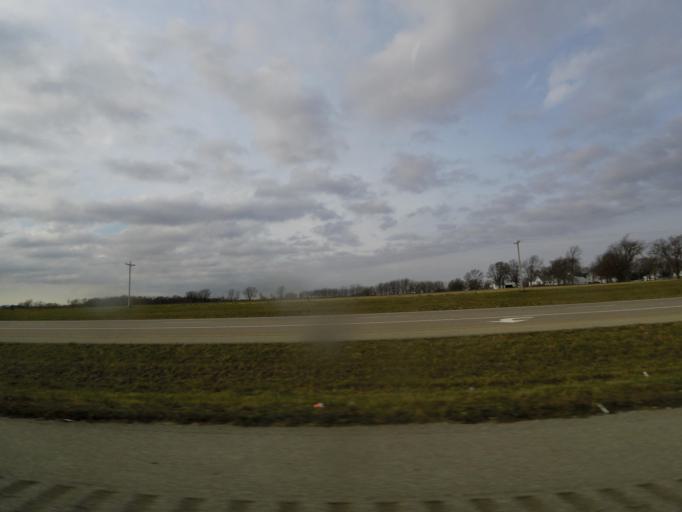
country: US
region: Illinois
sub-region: Christian County
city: Assumption
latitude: 39.4604
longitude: -89.0442
